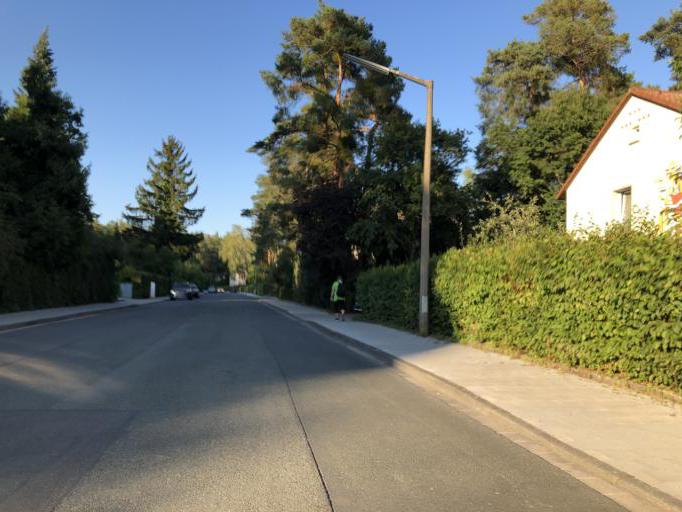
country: DE
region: Bavaria
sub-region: Regierungsbezirk Mittelfranken
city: Buckenhof
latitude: 49.6026
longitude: 11.0300
